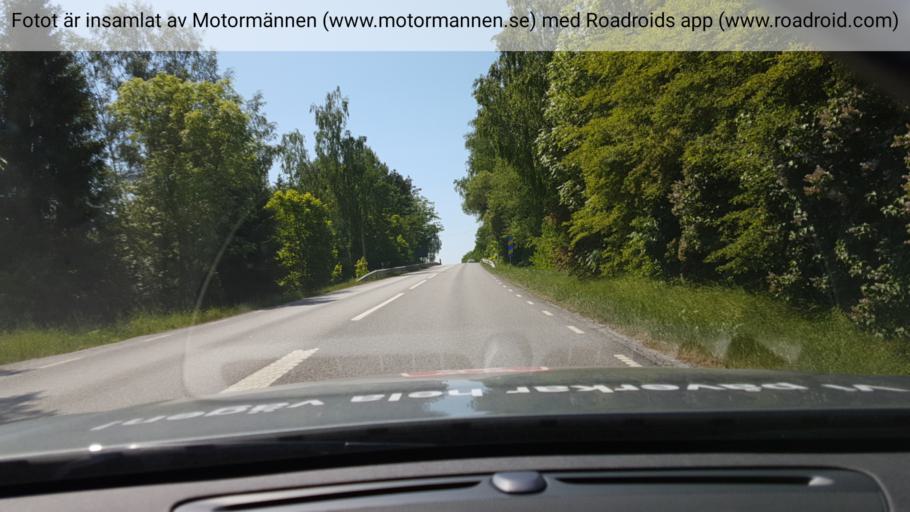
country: SE
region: Stockholm
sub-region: Norrtalje Kommun
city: Rimbo
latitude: 59.6874
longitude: 18.3712
